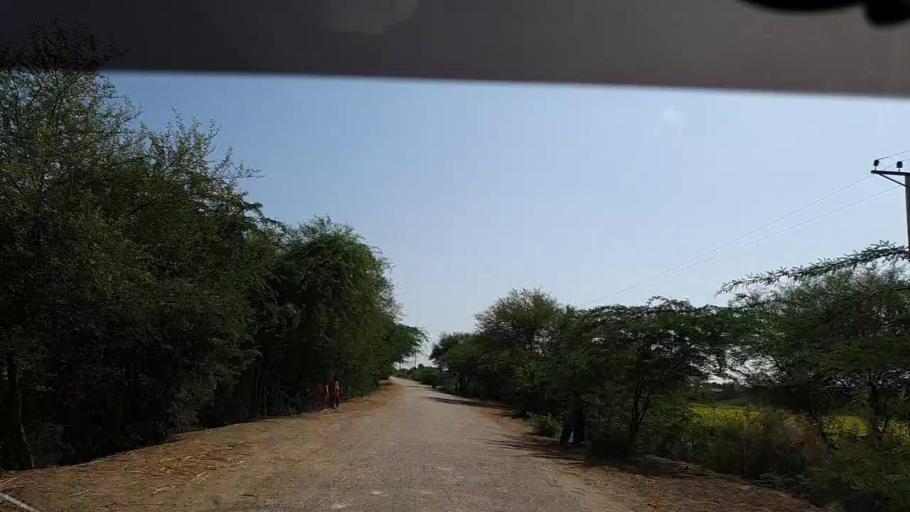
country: PK
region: Sindh
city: Badin
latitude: 24.6395
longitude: 68.7873
